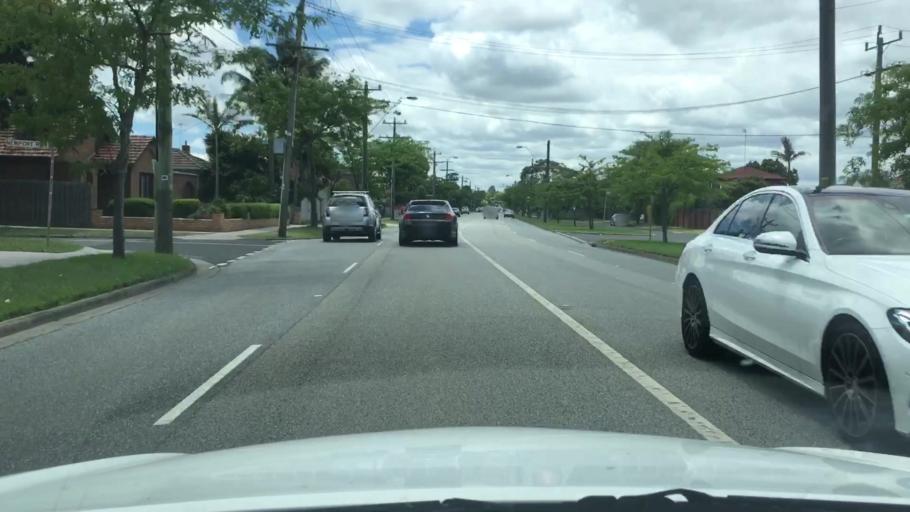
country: AU
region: Victoria
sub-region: Kingston
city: Clayton South
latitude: -37.9332
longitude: 145.1179
